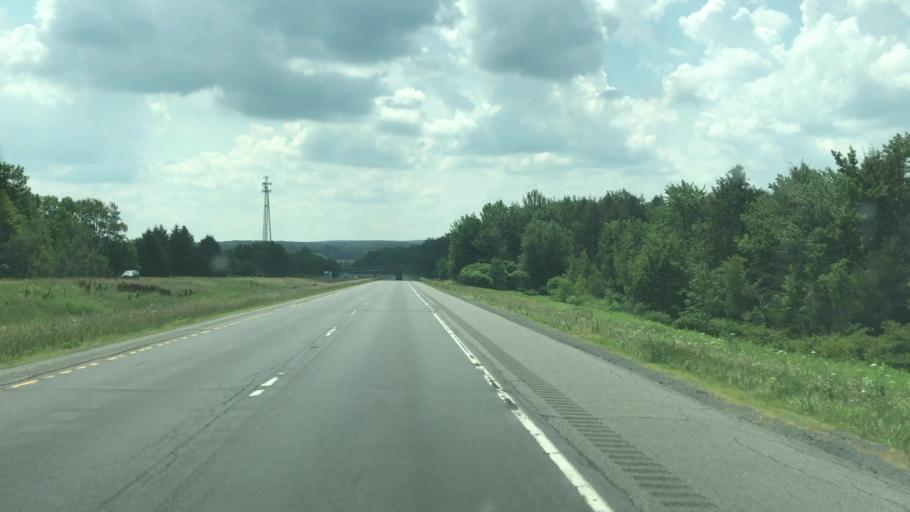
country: US
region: Pennsylvania
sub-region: Lackawanna County
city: Mount Cobb
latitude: 41.3772
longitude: -75.4536
